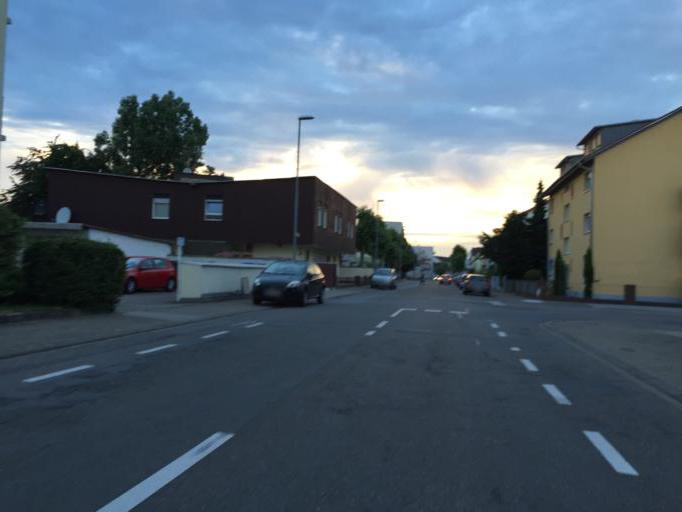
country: DE
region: Baden-Wuerttemberg
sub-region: Karlsruhe Region
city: Schwetzingen
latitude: 49.3814
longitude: 8.5824
